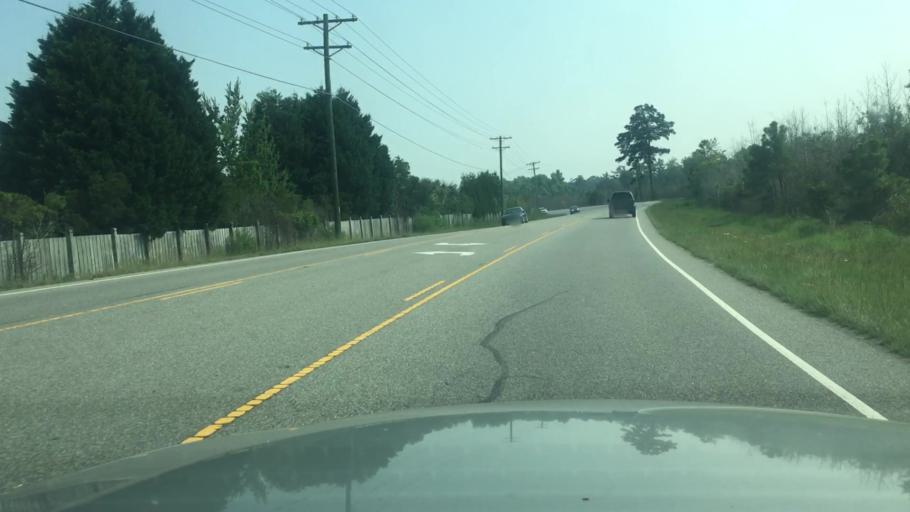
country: US
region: North Carolina
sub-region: Cumberland County
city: Hope Mills
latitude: 34.9205
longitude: -78.9104
